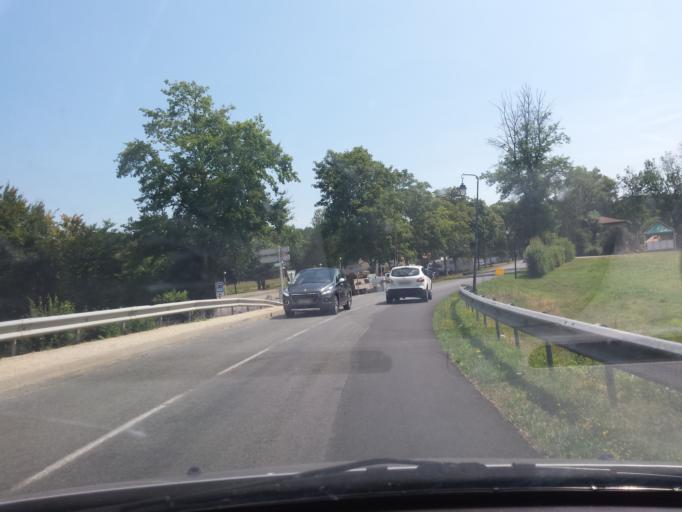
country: FR
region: Poitou-Charentes
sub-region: Departement de la Vienne
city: Availles-Limouzine
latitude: 46.1218
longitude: 0.6616
